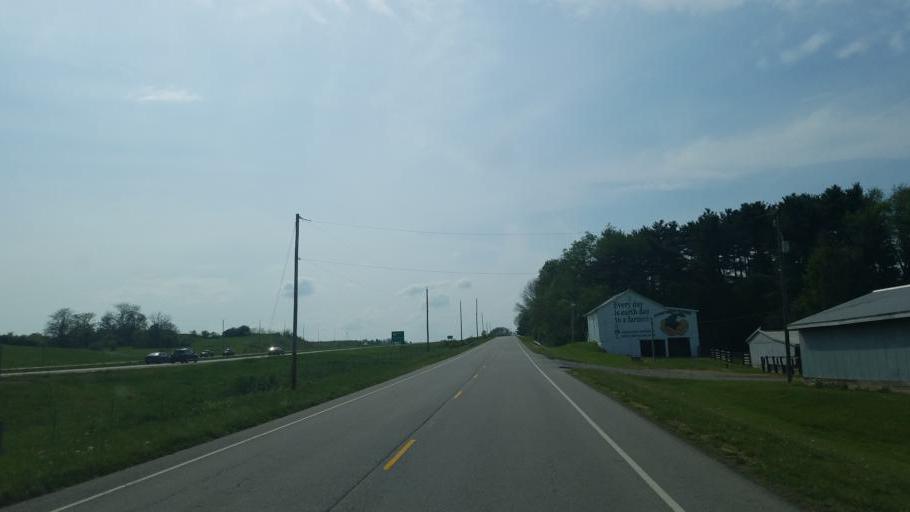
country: US
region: Ohio
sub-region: Licking County
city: Granville South
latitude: 40.0721
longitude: -82.5774
